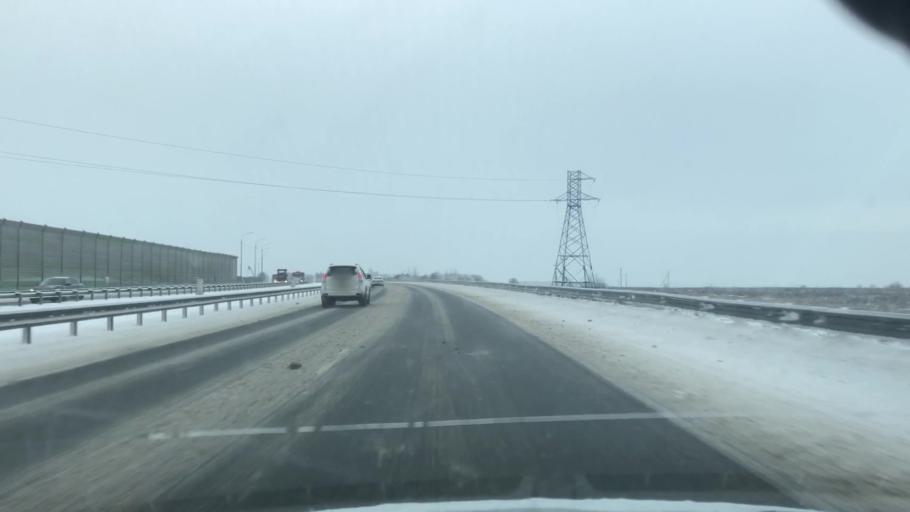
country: RU
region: Moskovskaya
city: Mikhnevo
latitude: 55.1186
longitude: 37.9283
